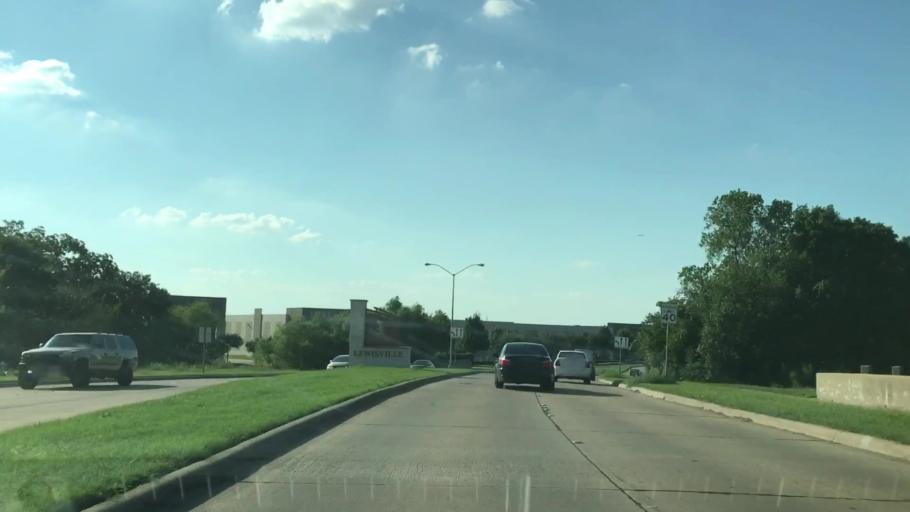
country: US
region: Texas
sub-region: Dallas County
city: Coppell
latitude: 32.9952
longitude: -97.0046
